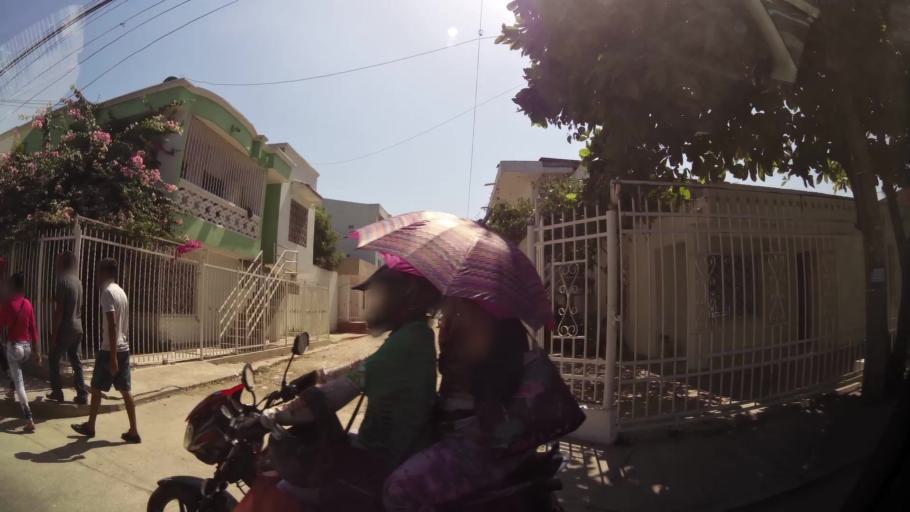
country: CO
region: Bolivar
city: Cartagena
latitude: 10.3851
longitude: -75.4606
